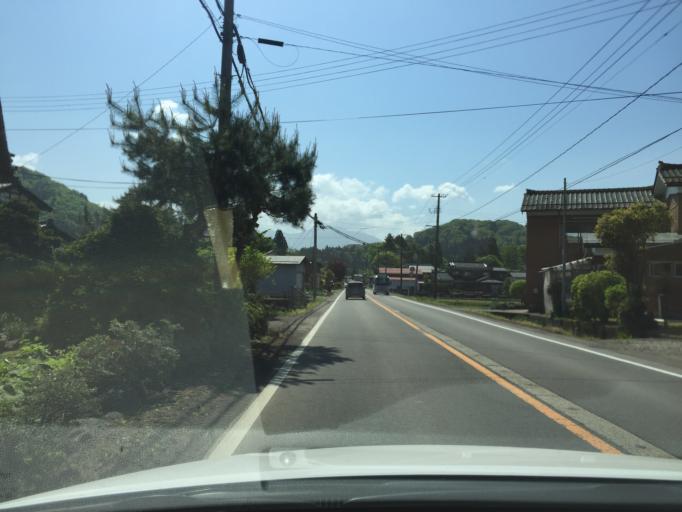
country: JP
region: Niigata
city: Kamo
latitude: 37.6306
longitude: 139.0949
